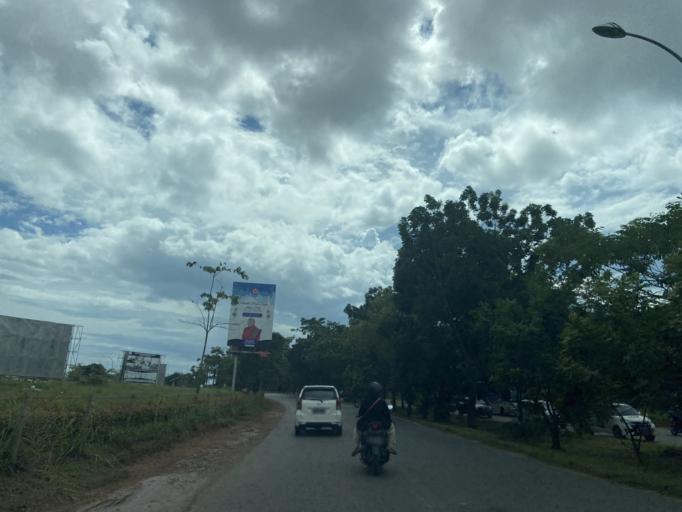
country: SG
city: Singapore
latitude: 1.0437
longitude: 103.9802
